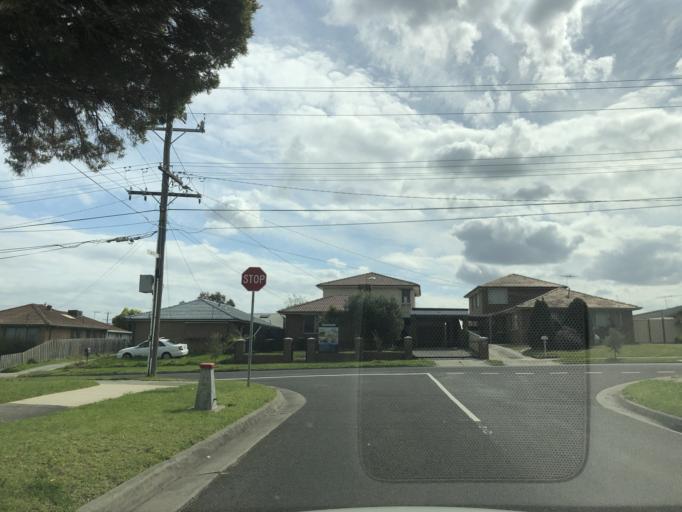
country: AU
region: Victoria
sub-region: Greater Dandenong
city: Noble Park North
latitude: -37.9547
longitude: 145.1995
